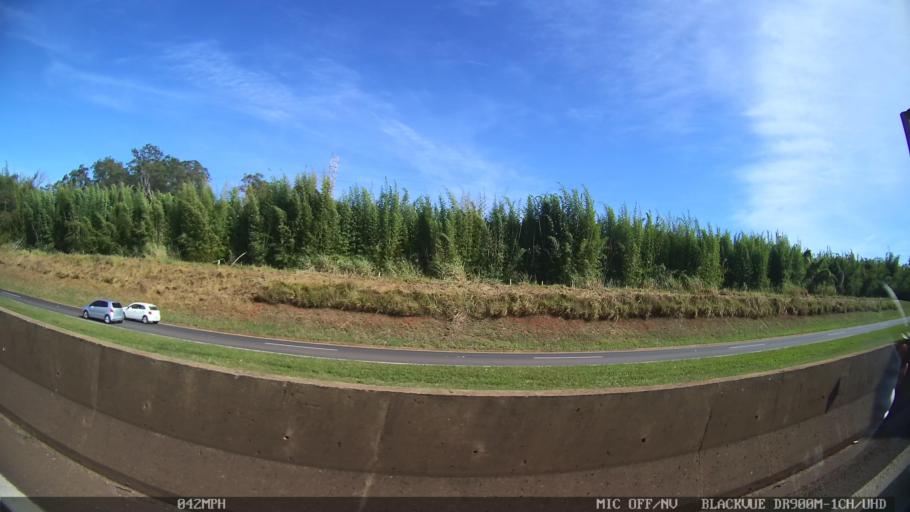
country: BR
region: Sao Paulo
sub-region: Leme
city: Leme
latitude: -22.2709
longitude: -47.3917
